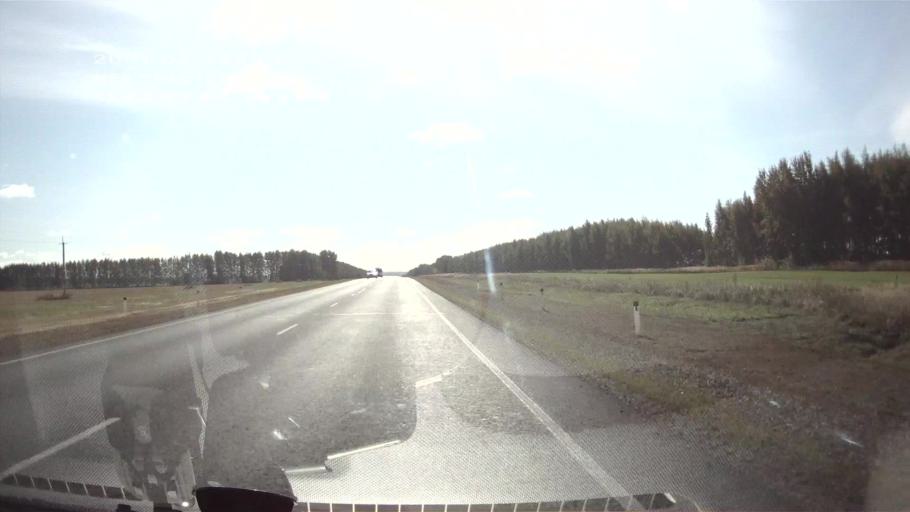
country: RU
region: Ulyanovsk
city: Tsil'na
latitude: 54.5539
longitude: 47.9371
